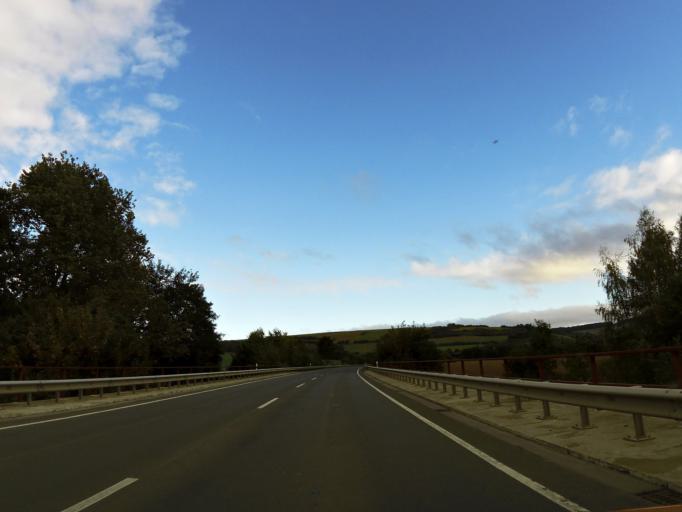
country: DE
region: Lower Saxony
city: Einbeck
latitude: 51.8277
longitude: 9.8304
